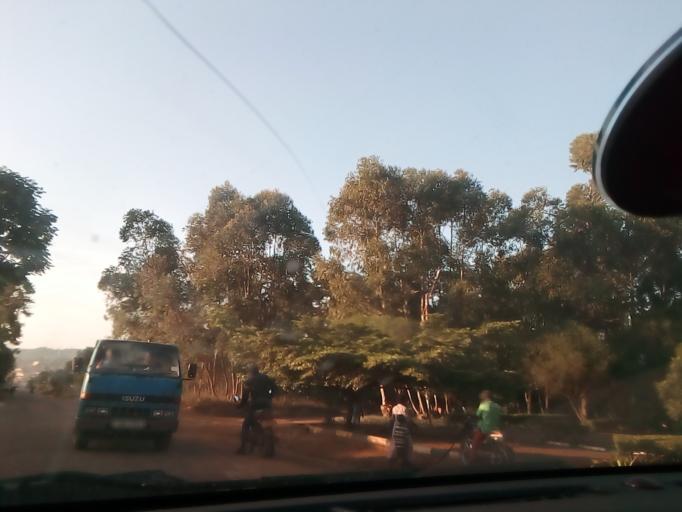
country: UG
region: Central Region
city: Masaka
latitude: -0.3306
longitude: 31.7610
